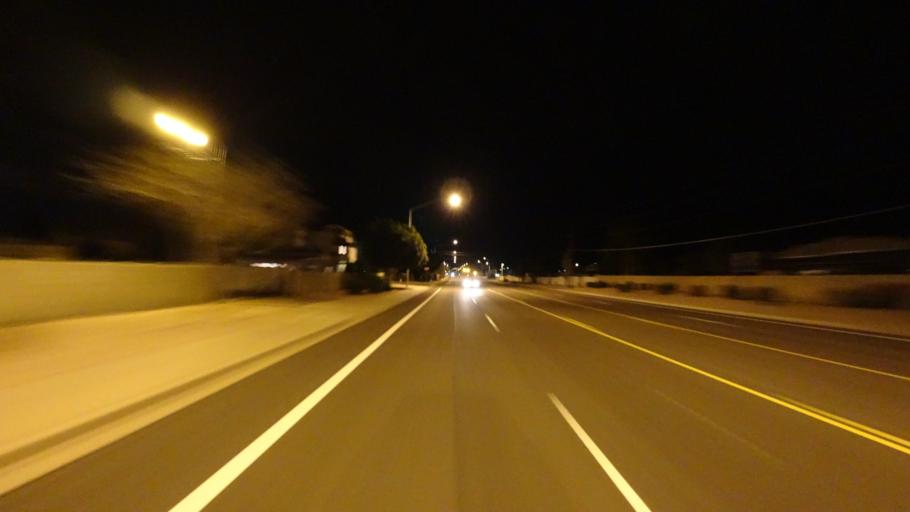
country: US
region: Arizona
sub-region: Maricopa County
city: Mesa
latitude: 33.4634
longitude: -111.7014
